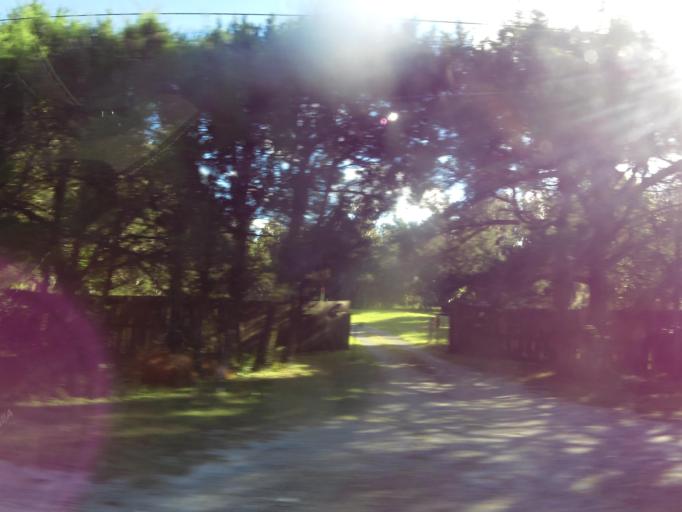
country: US
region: Florida
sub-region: Marion County
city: Citra
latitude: 29.4863
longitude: -82.1670
